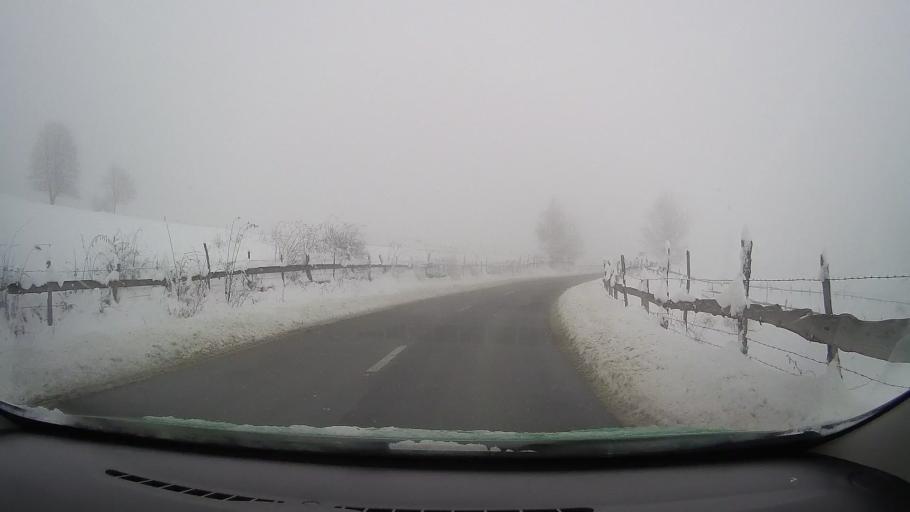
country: RO
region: Sibiu
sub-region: Comuna Jina
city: Jina
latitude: 45.7884
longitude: 23.6980
